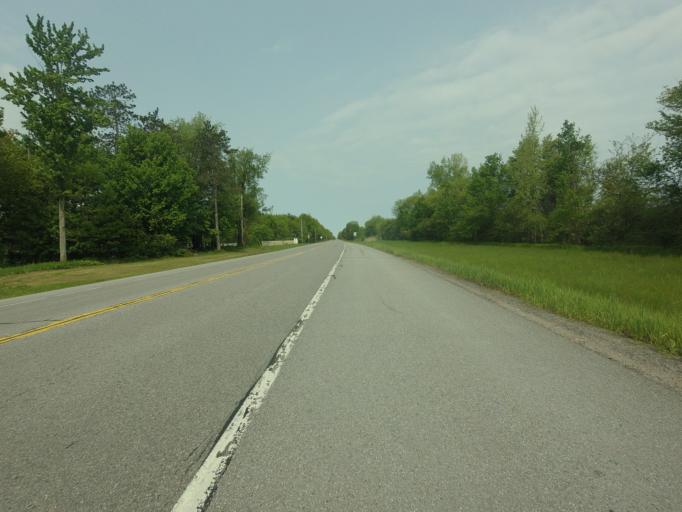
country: US
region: New York
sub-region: Jefferson County
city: Dexter
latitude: 44.0143
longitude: -76.0221
